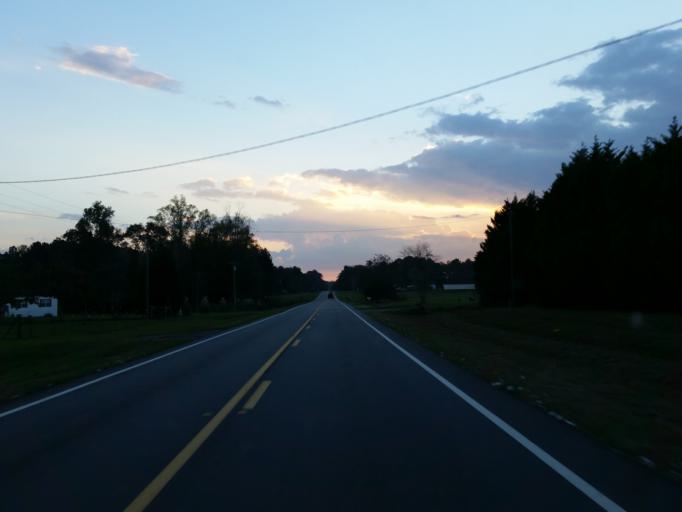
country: US
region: Georgia
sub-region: Pulaski County
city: Hawkinsville
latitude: 32.2276
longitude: -83.5163
